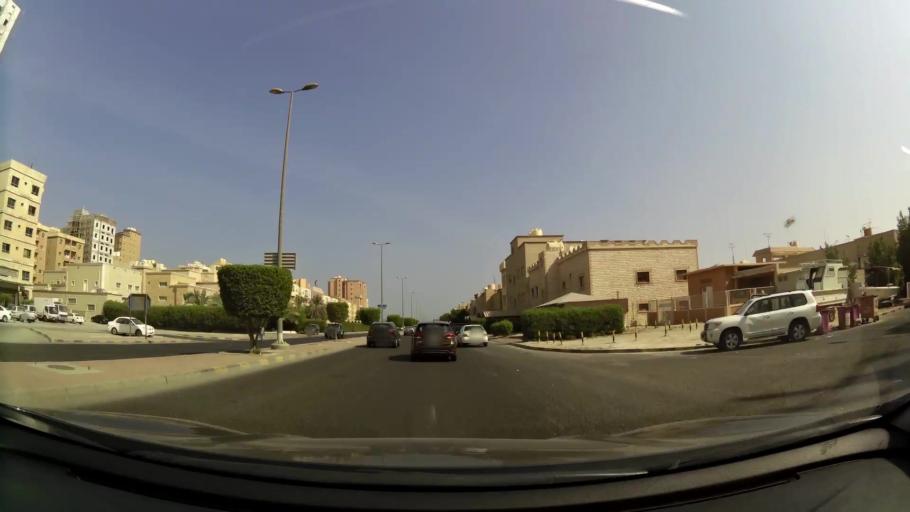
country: KW
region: Al Ahmadi
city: Al Manqaf
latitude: 29.0918
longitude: 48.1324
